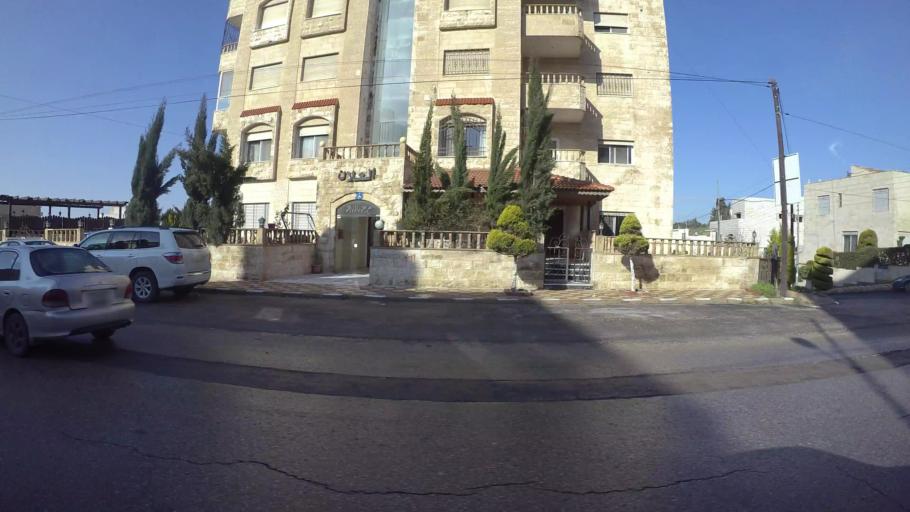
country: JO
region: Amman
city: Al Jubayhah
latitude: 32.0095
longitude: 35.8500
